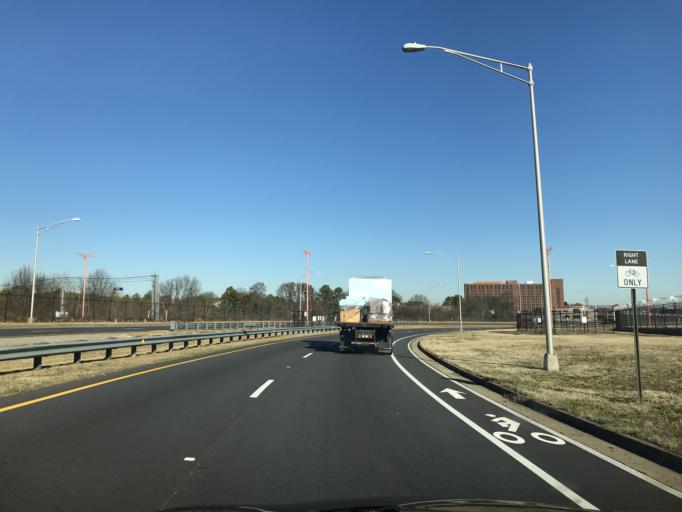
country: US
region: Georgia
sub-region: Fulton County
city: College Park
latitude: 33.6197
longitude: -84.4522
